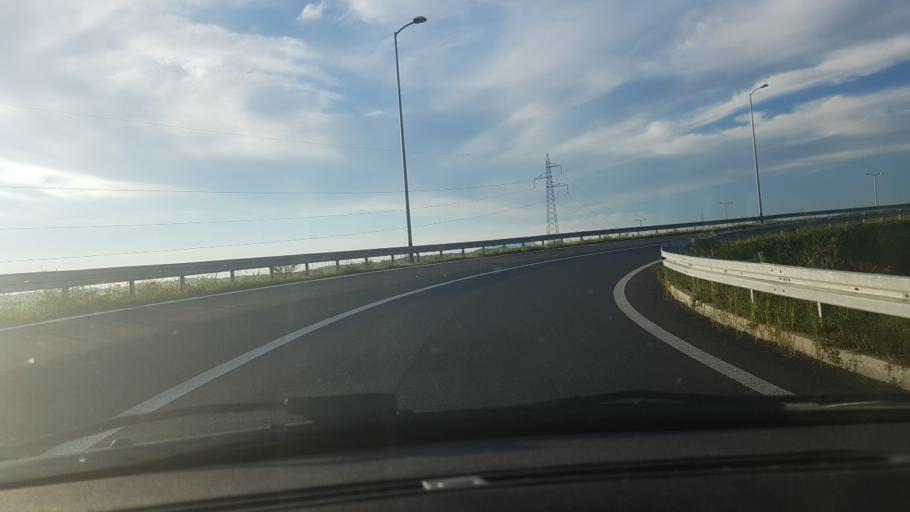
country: HR
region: Krapinsko-Zagorska
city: Selnica
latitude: 46.0363
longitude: 16.0744
